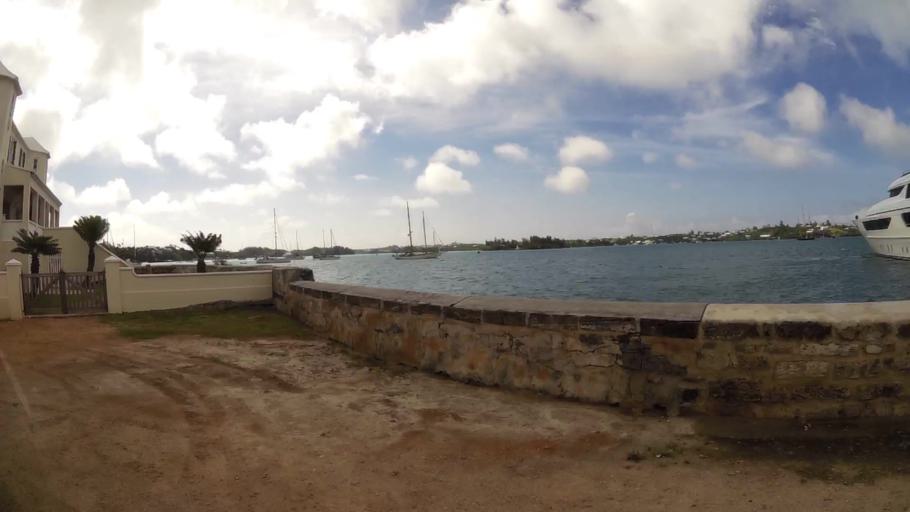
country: BM
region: Saint George
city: Saint George
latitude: 32.3802
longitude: -64.6759
